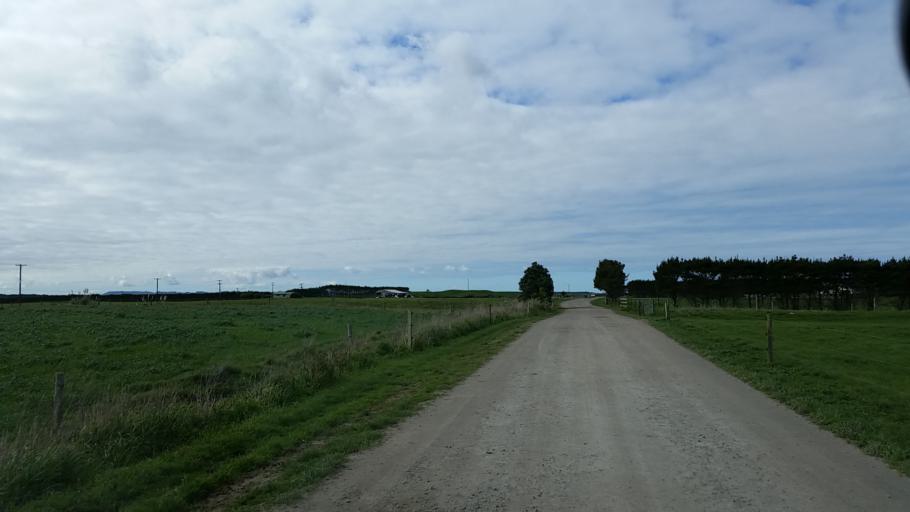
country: NZ
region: Taranaki
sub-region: South Taranaki District
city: Patea
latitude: -39.8251
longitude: 174.6544
